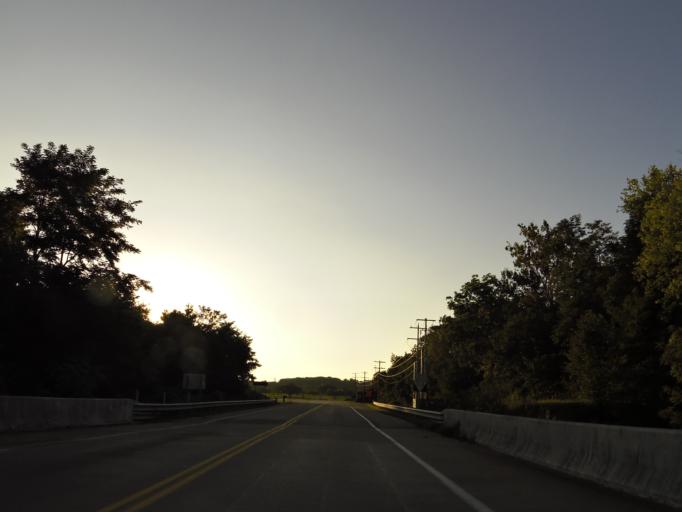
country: US
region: Tennessee
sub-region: Jefferson County
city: Dandridge
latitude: 36.0421
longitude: -83.3420
